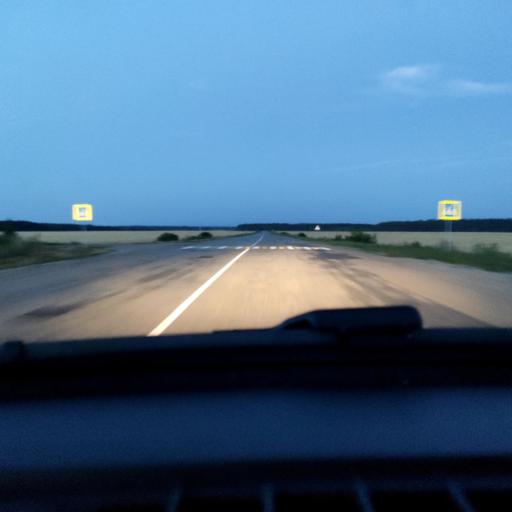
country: RU
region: Lipetsk
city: Zadonsk
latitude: 52.2995
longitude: 38.8027
